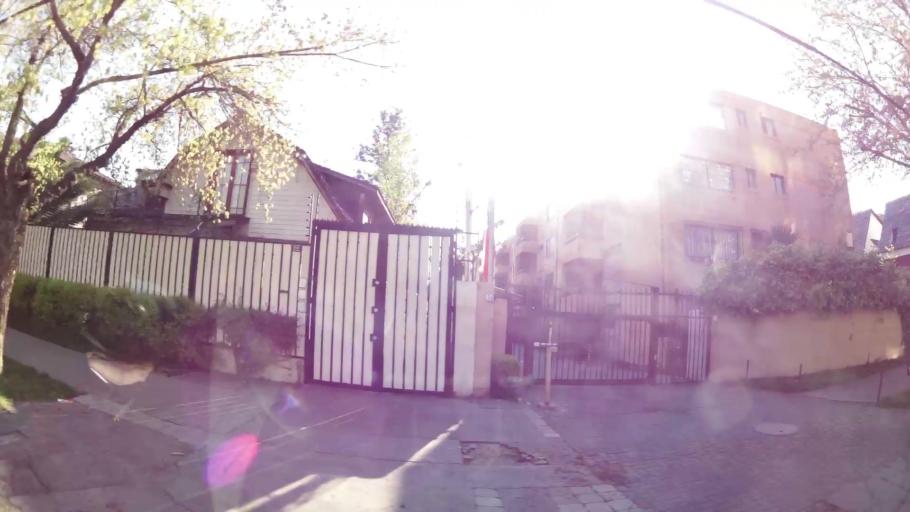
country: CL
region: Santiago Metropolitan
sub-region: Provincia de Santiago
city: Villa Presidente Frei, Nunoa, Santiago, Chile
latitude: -33.4504
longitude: -70.5960
